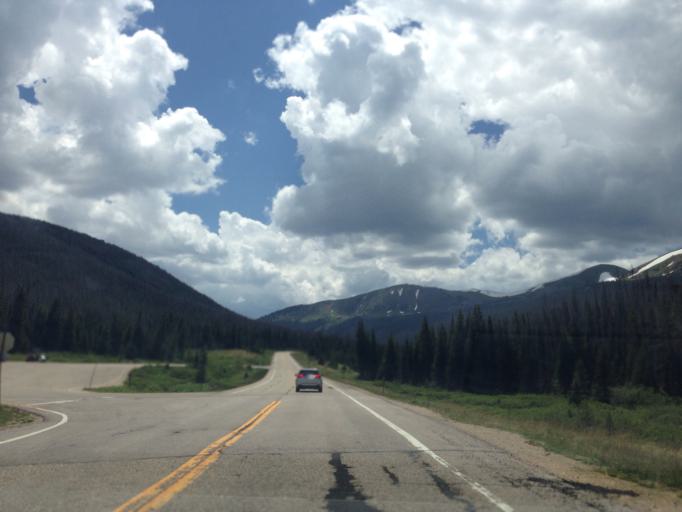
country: US
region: Colorado
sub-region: Larimer County
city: Estes Park
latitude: 40.5407
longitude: -105.8823
